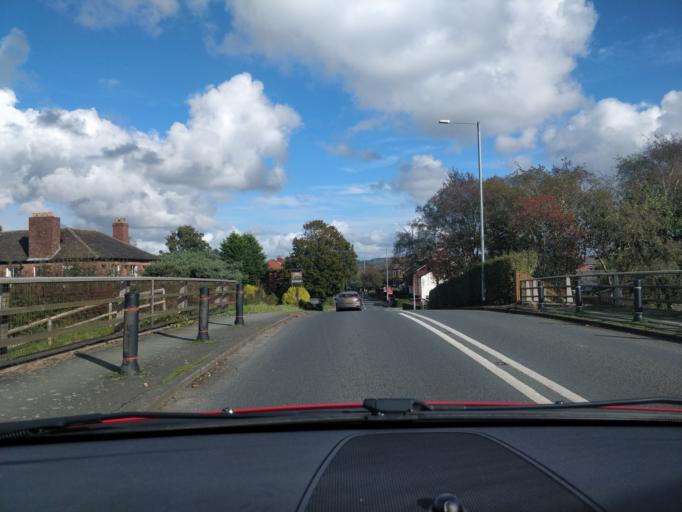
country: GB
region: England
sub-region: Lancashire
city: Parbold
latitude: 53.5922
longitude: -2.8192
